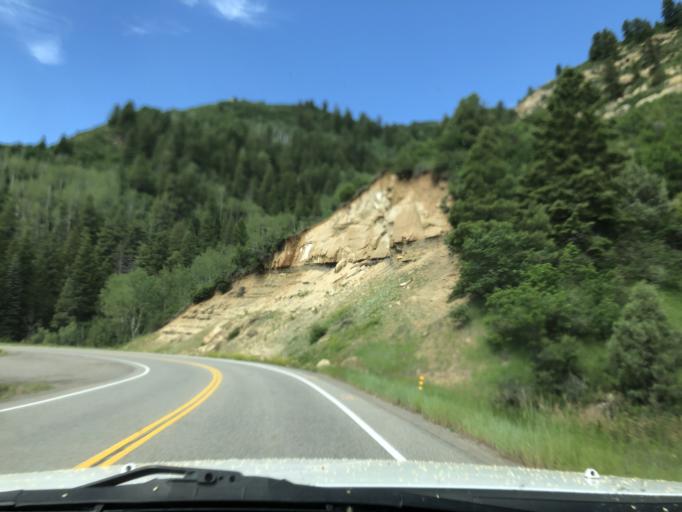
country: US
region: Colorado
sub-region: Delta County
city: Paonia
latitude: 38.9570
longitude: -107.3431
